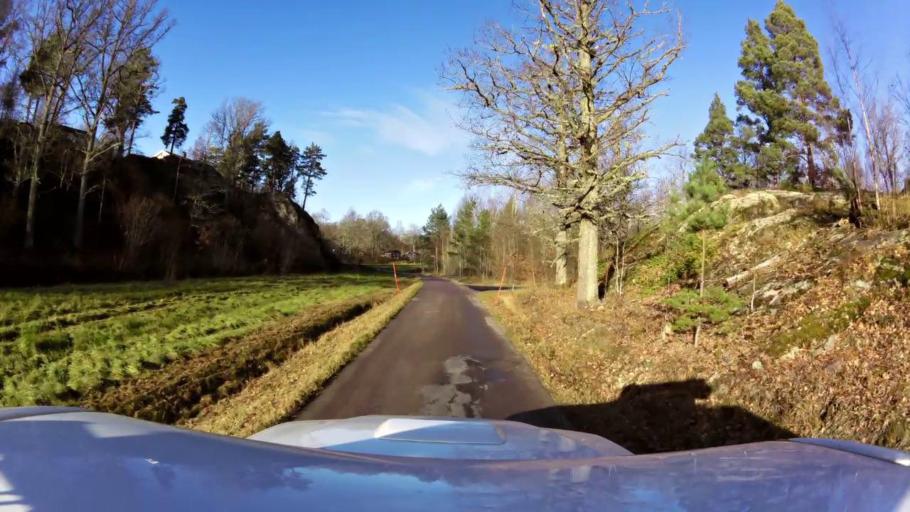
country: SE
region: OEstergoetland
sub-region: Linkopings Kommun
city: Sturefors
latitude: 58.2546
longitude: 15.7053
